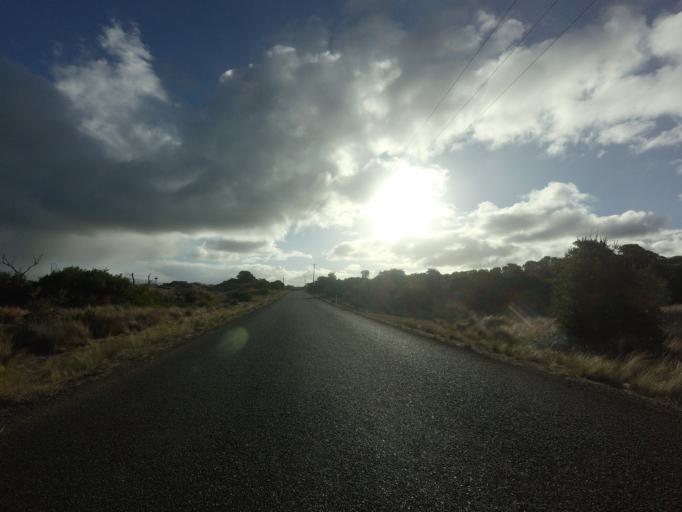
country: AU
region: Tasmania
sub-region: Break O'Day
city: St Helens
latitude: -42.0885
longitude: 148.1506
